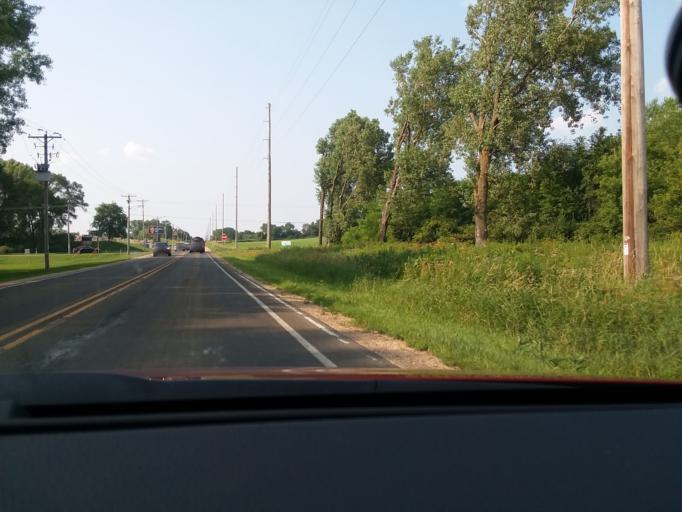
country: US
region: Wisconsin
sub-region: Dane County
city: Sun Prairie
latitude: 43.1422
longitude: -89.2659
